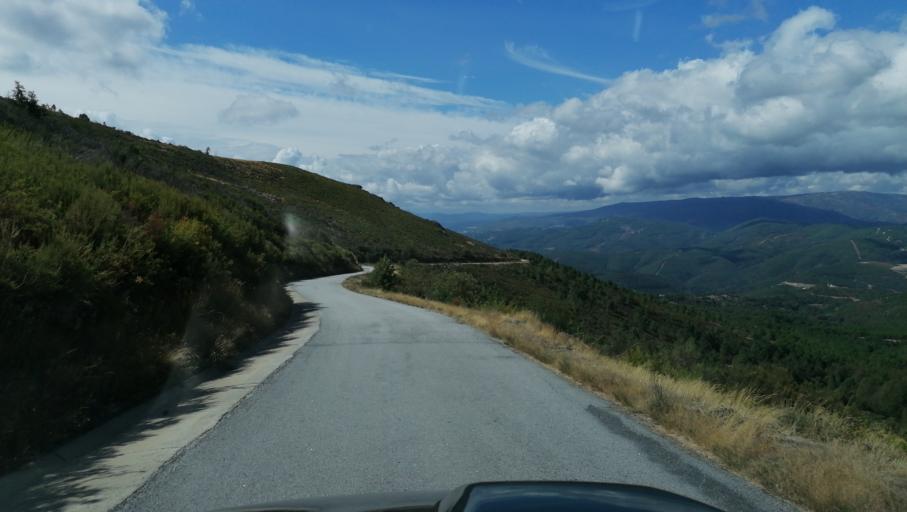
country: PT
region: Vila Real
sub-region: Vila Pouca de Aguiar
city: Vila Pouca de Aguiar
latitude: 41.5603
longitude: -7.6917
